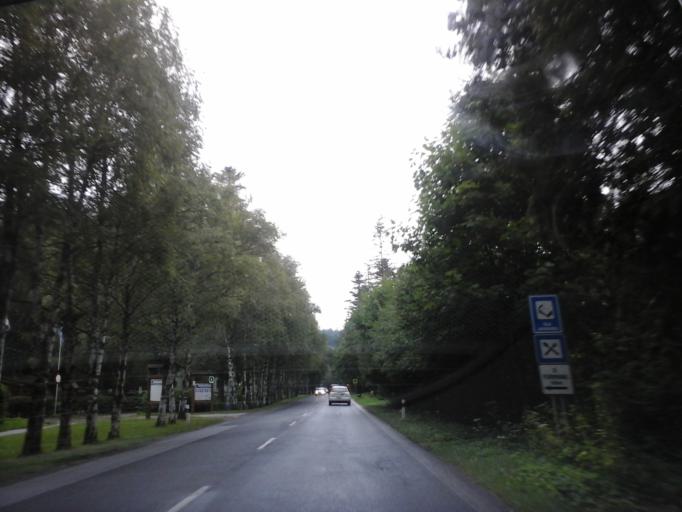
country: SK
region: Presovsky
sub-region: Okres Poprad
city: Zdiar
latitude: 49.2276
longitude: 20.3203
